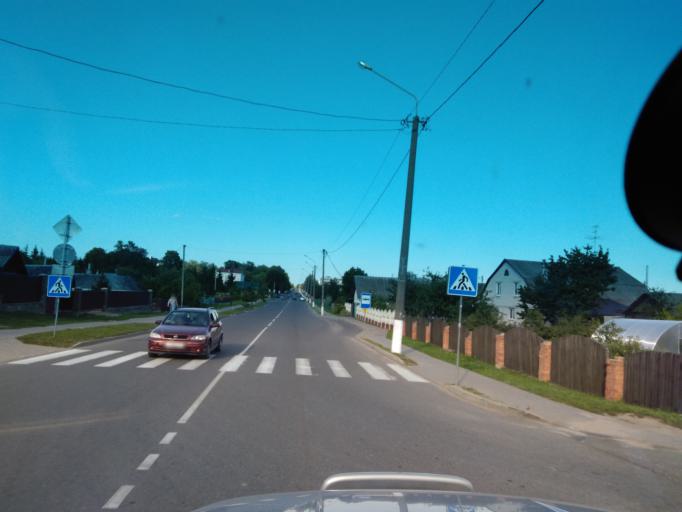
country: BY
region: Minsk
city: Dzyarzhynsk
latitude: 53.6801
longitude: 27.1204
